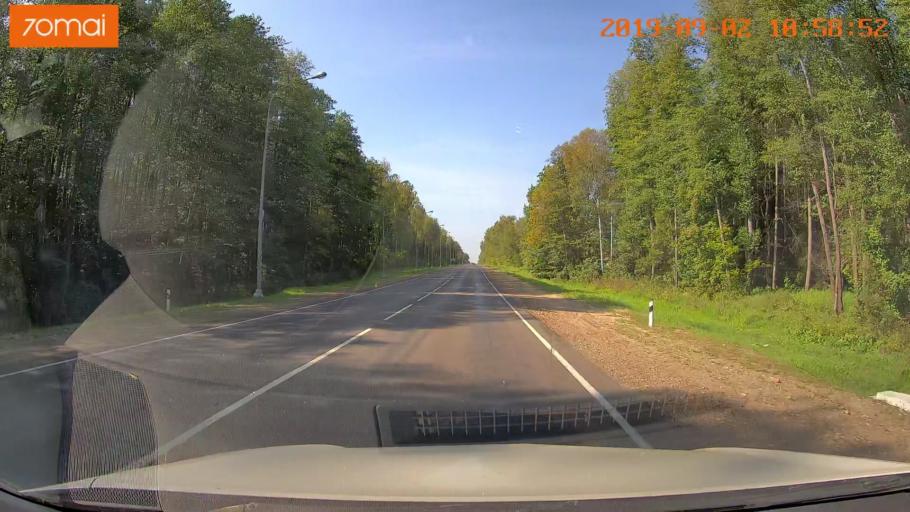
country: RU
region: Smolensk
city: Yekimovichi
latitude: 54.1611
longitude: 33.4496
